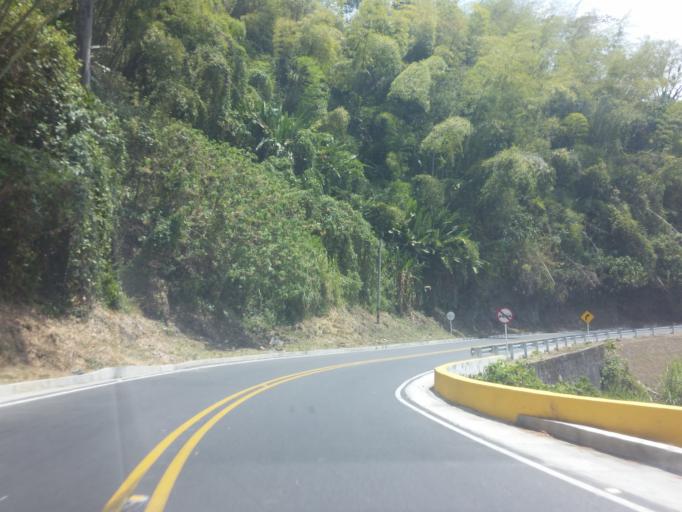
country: CO
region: Caldas
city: Chinchina
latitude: 4.9882
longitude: -75.5898
